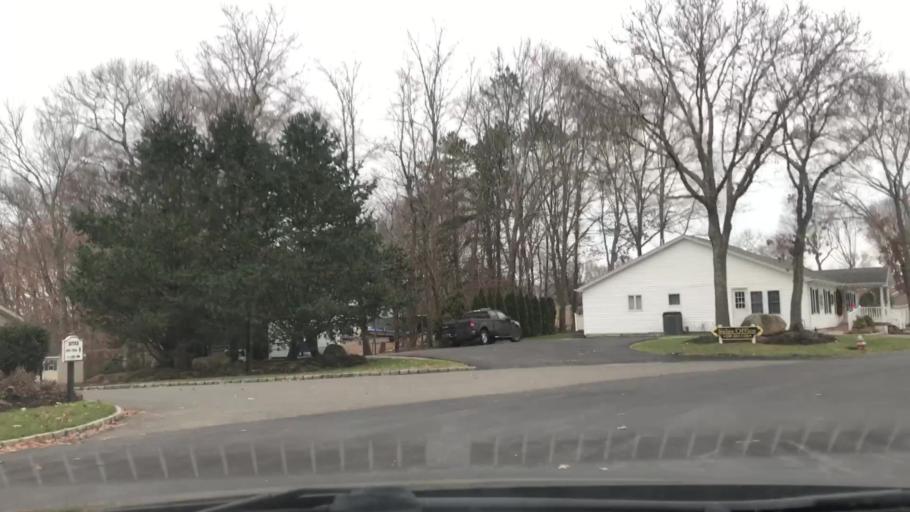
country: US
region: New York
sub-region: Suffolk County
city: Baiting Hollow
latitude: 40.9335
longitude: -72.7091
